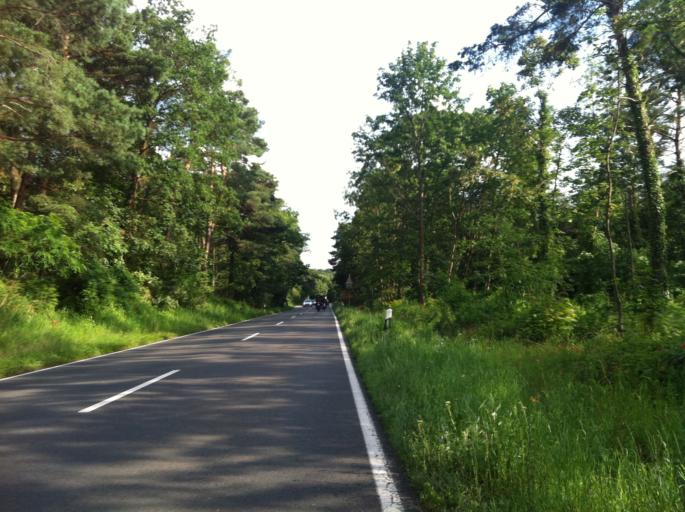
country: DE
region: Rheinland-Pfalz
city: Budenheim
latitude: 50.0103
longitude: 8.1693
